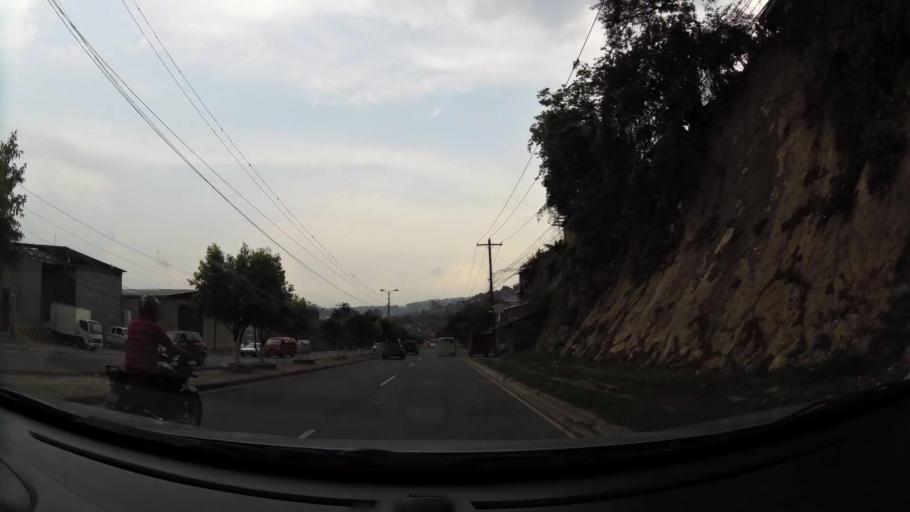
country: HN
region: Francisco Morazan
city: El Lolo
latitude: 14.1002
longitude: -87.2409
